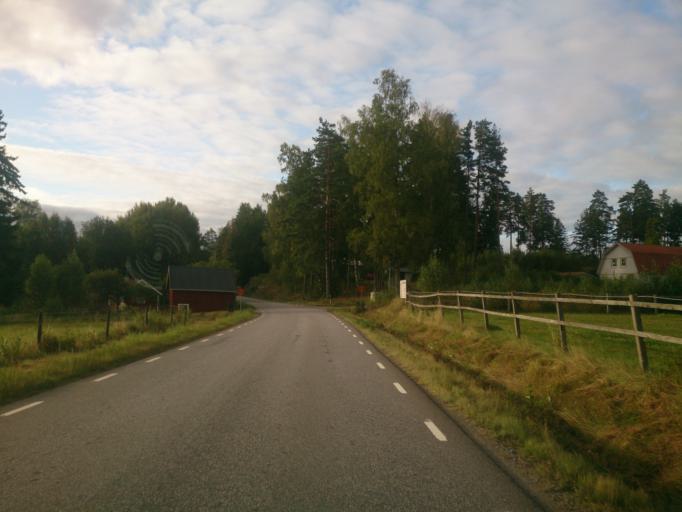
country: SE
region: OEstergoetland
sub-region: Linkopings Kommun
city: Sturefors
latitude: 58.3129
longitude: 15.8715
